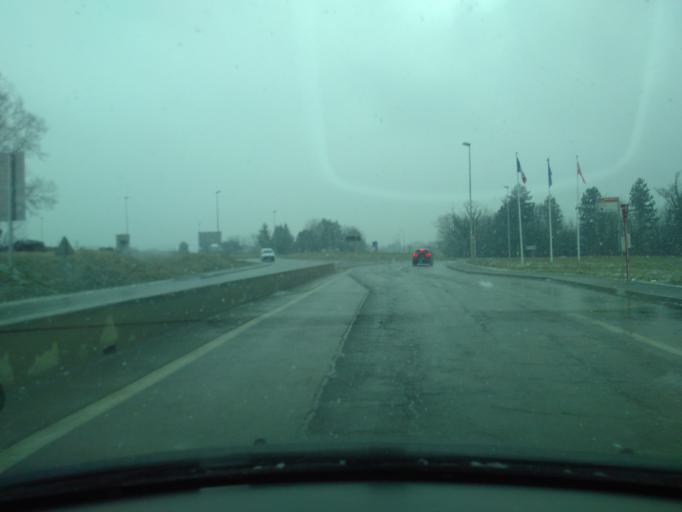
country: FR
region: Rhone-Alpes
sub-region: Departement de la Haute-Savoie
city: Neydens
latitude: 46.1290
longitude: 6.0901
